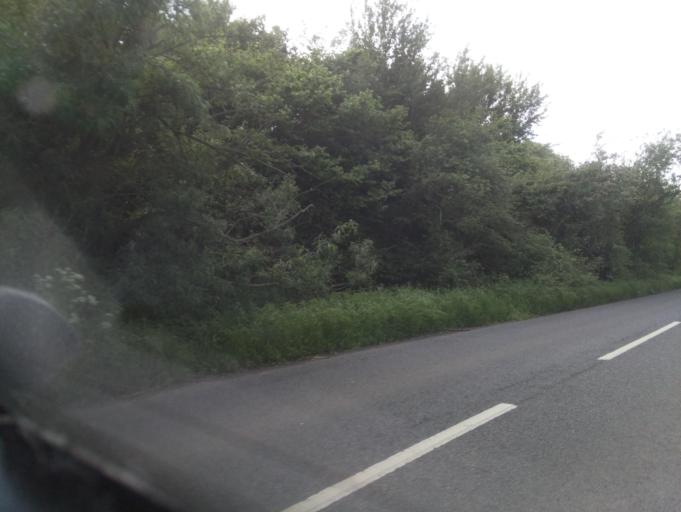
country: GB
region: England
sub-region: Gloucestershire
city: Chipping Campden
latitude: 52.0485
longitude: -1.7456
